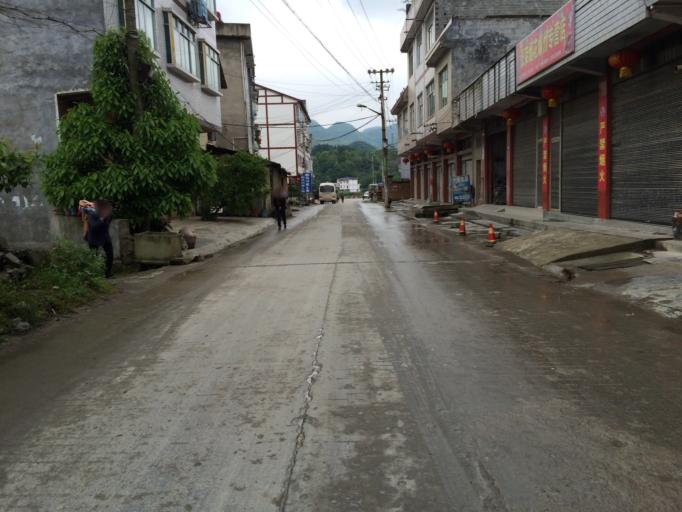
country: CN
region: Guizhou Sheng
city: Dalucao
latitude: 27.8344
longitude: 107.2533
